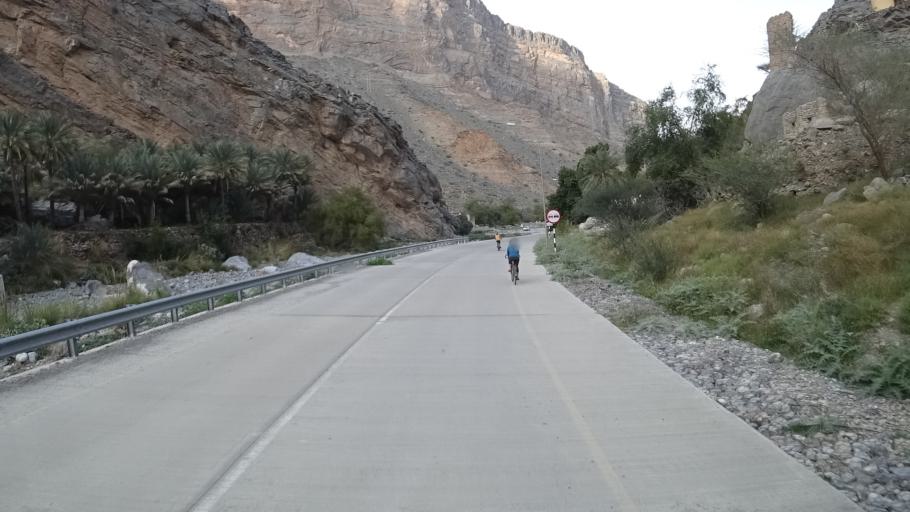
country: OM
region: Al Batinah
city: Bayt al `Awabi
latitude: 23.3131
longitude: 57.4803
